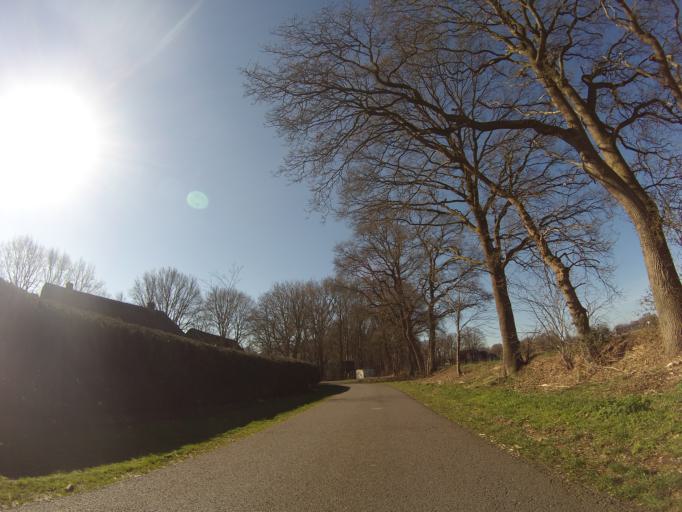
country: NL
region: Drenthe
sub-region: Gemeente Coevorden
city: Sleen
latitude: 52.7585
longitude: 6.8271
